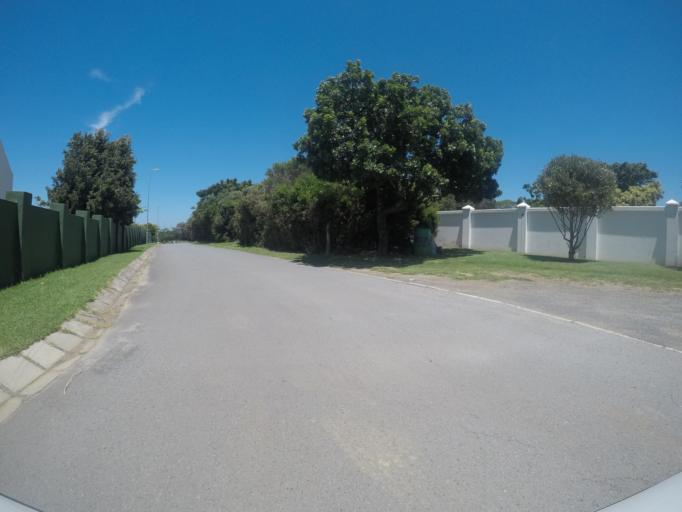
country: ZA
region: Eastern Cape
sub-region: Buffalo City Metropolitan Municipality
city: East London
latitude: -32.9350
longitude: 28.0011
